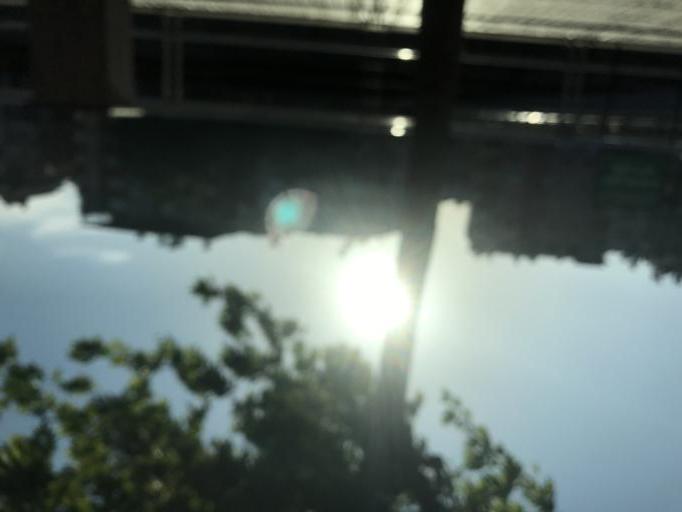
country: TR
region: Hatay
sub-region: Antakya Ilcesi
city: Antakya
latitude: 36.2045
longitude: 36.1621
